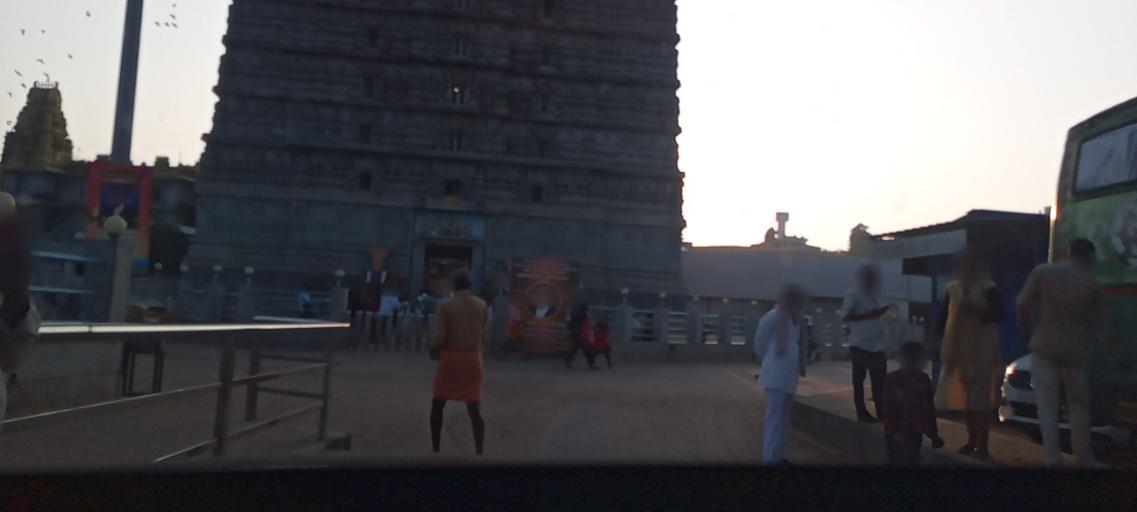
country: IN
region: Karnataka
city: Murudeshwara
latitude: 14.0944
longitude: 74.4856
